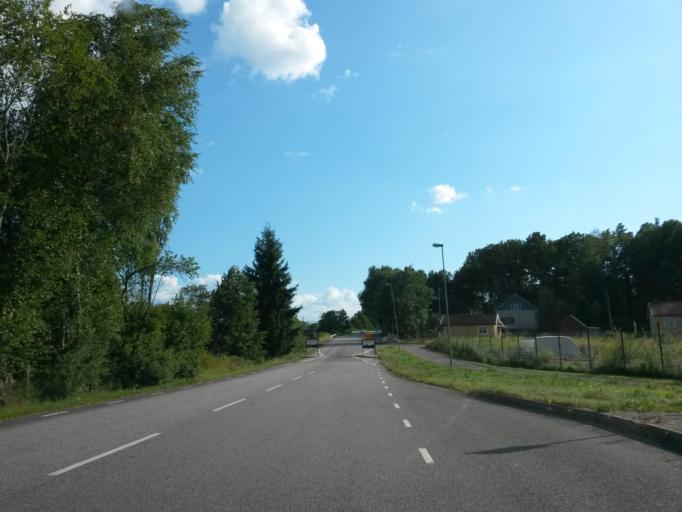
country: SE
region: Vaestra Goetaland
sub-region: Lerums Kommun
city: Stenkullen
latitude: 57.7946
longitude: 12.3176
